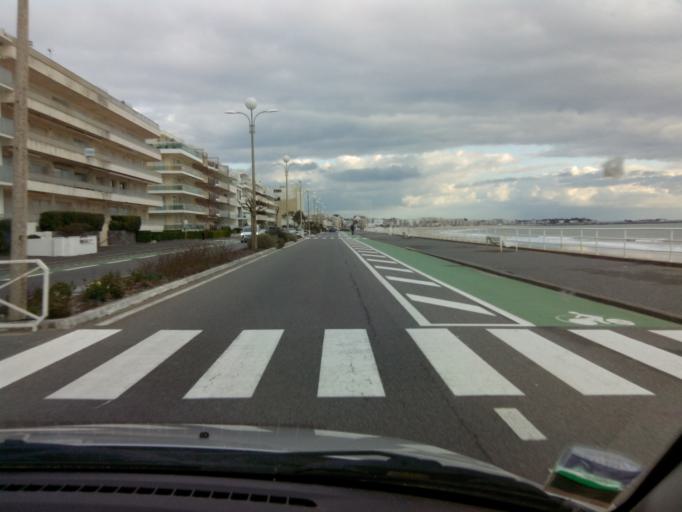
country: FR
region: Pays de la Loire
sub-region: Departement de la Loire-Atlantique
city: La Baule-Escoublac
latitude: 47.2757
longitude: -2.3638
